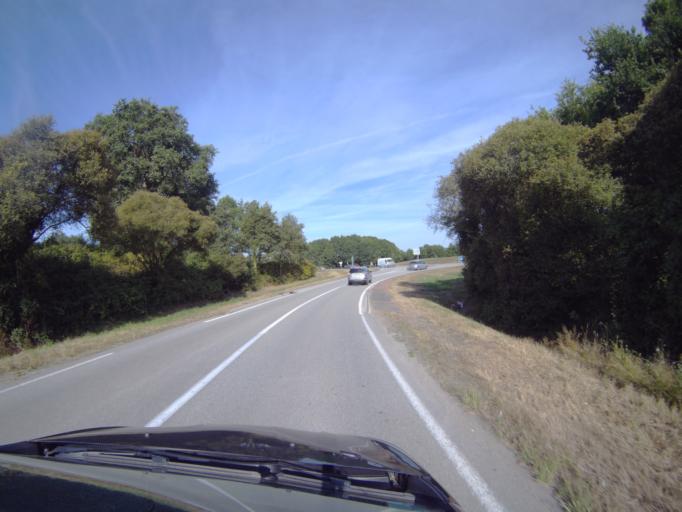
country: FR
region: Pays de la Loire
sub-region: Departement de la Vendee
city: Les Clouzeaux
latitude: 46.6485
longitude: -1.5107
